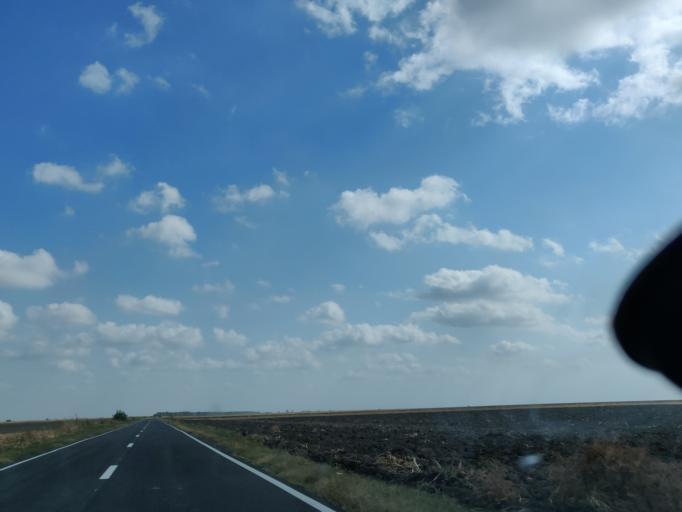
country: RO
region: Vrancea
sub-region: Comuna Ciorasti
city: Mihalceni
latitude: 45.4426
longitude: 27.3399
